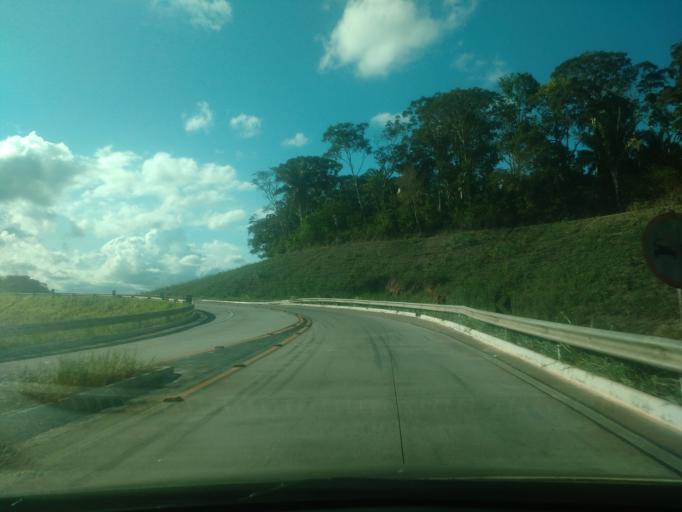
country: BR
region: Alagoas
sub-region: Messias
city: Messias
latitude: -9.3690
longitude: -35.8307
